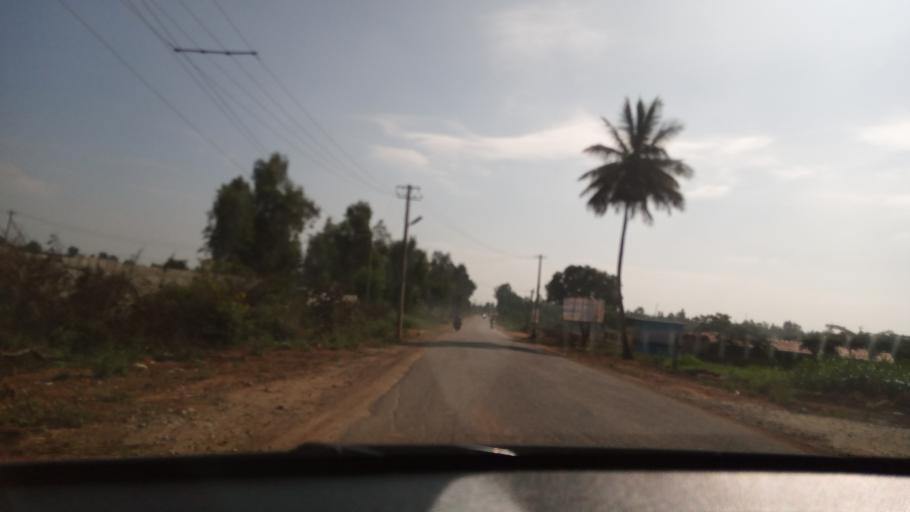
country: IN
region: Karnataka
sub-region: Bangalore Rural
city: Vijayapura
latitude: 13.2891
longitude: 77.7836
